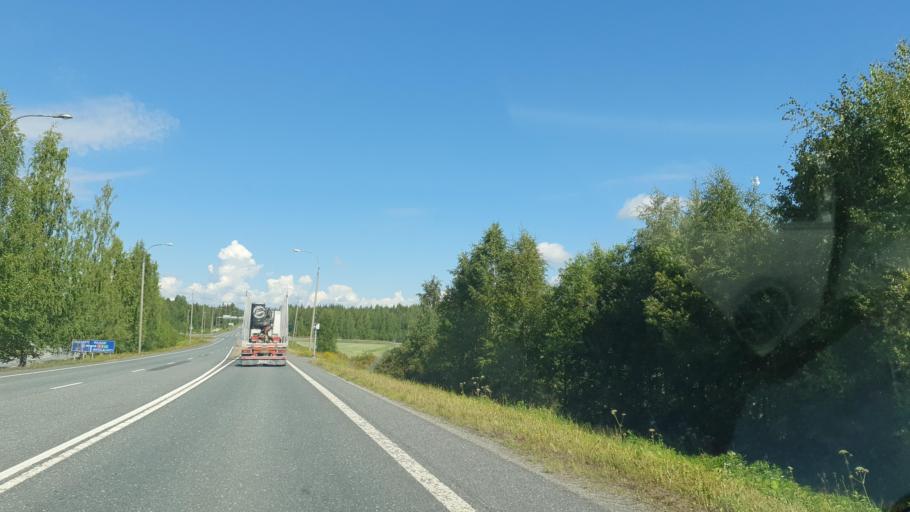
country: FI
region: Northern Savo
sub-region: Ylae-Savo
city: Iisalmi
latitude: 63.6241
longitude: 27.2249
